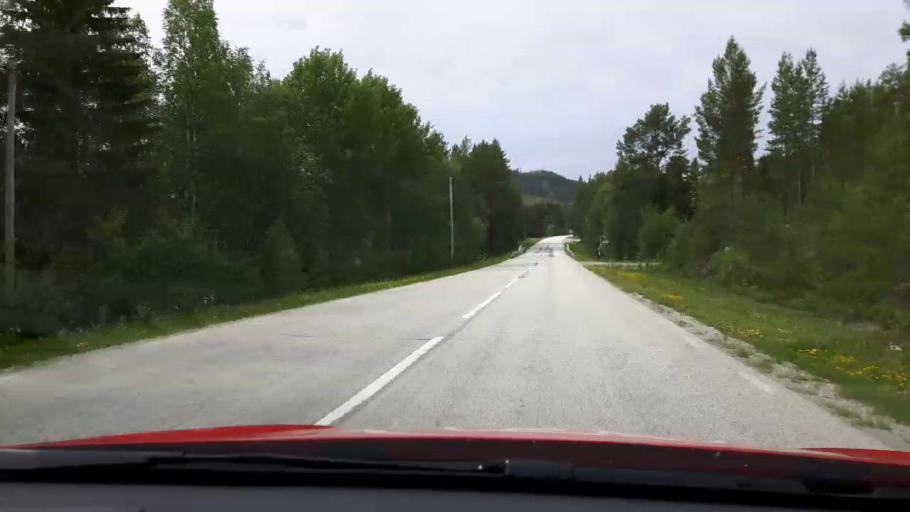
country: SE
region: Jaemtland
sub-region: Harjedalens Kommun
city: Sveg
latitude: 62.4120
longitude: 13.6418
